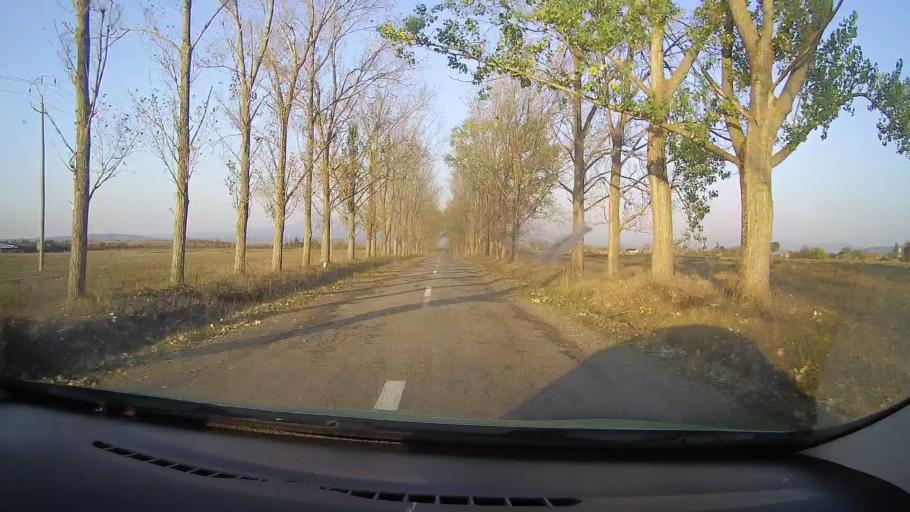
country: RO
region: Arad
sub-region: Comuna Barsa
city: Barsa
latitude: 46.3833
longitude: 22.0620
